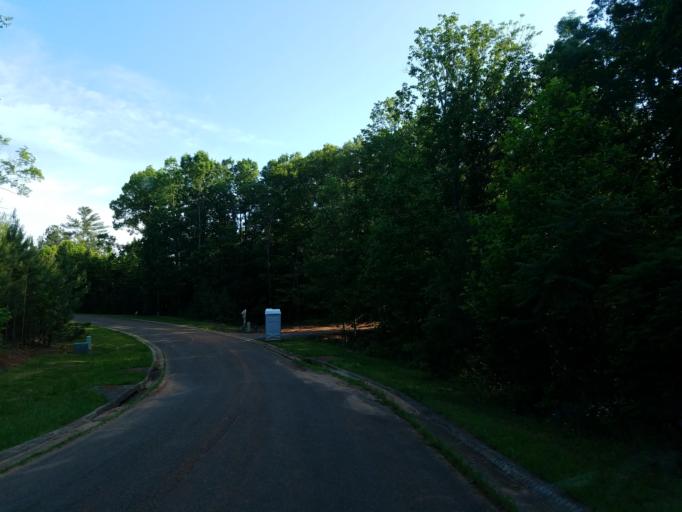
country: US
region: Georgia
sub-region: Pickens County
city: Nelson
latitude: 34.3853
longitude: -84.3255
